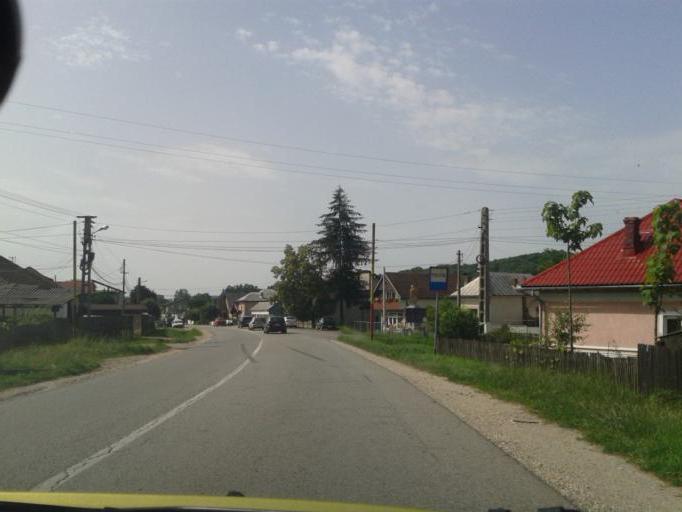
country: RO
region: Valcea
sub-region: Comuna Pietrari
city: Pietrarii de Sus
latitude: 45.1118
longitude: 24.1143
